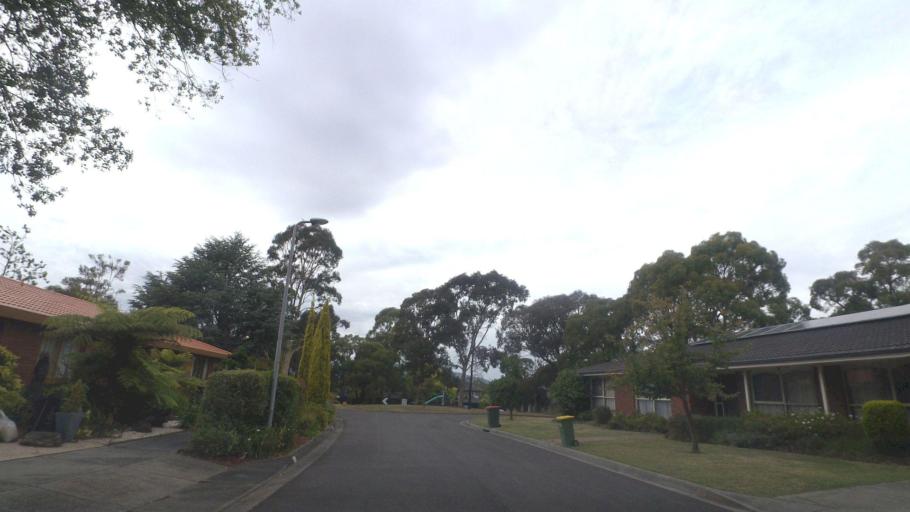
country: AU
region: Victoria
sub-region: Knox
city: Wantirna
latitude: -37.8527
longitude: 145.2369
